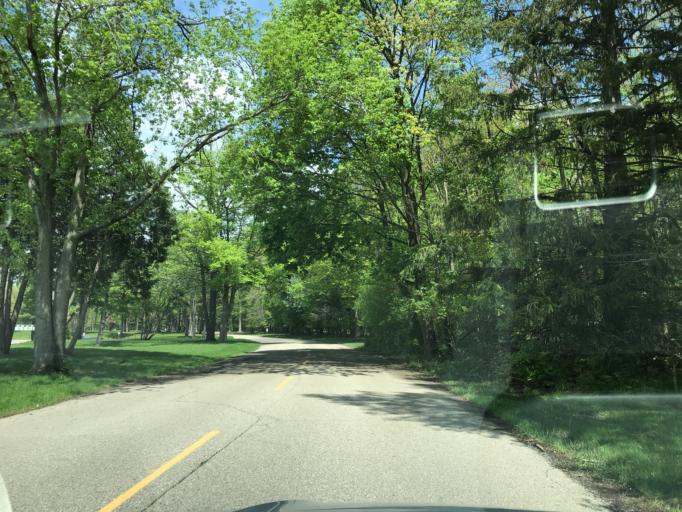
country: US
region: Michigan
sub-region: Oakland County
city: Franklin
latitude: 42.4757
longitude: -83.3012
